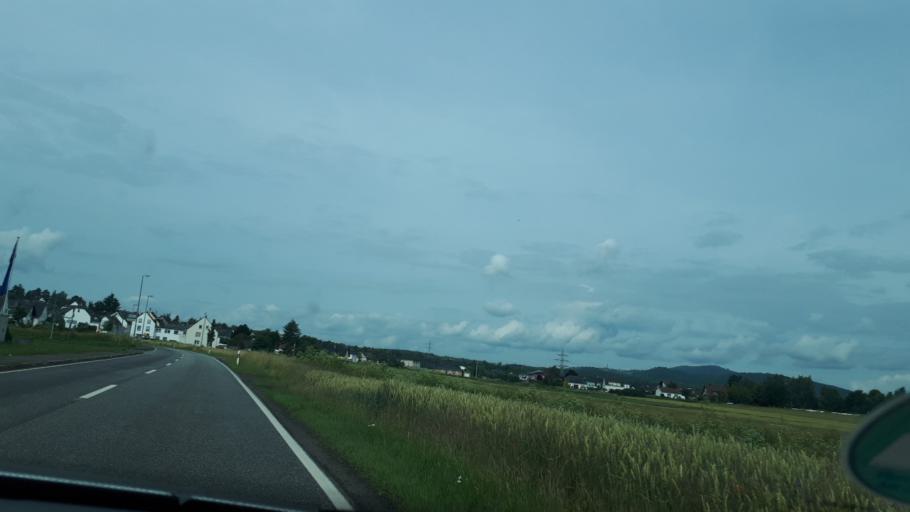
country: DE
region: Rheinland-Pfalz
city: Thur
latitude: 50.3323
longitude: 7.2775
